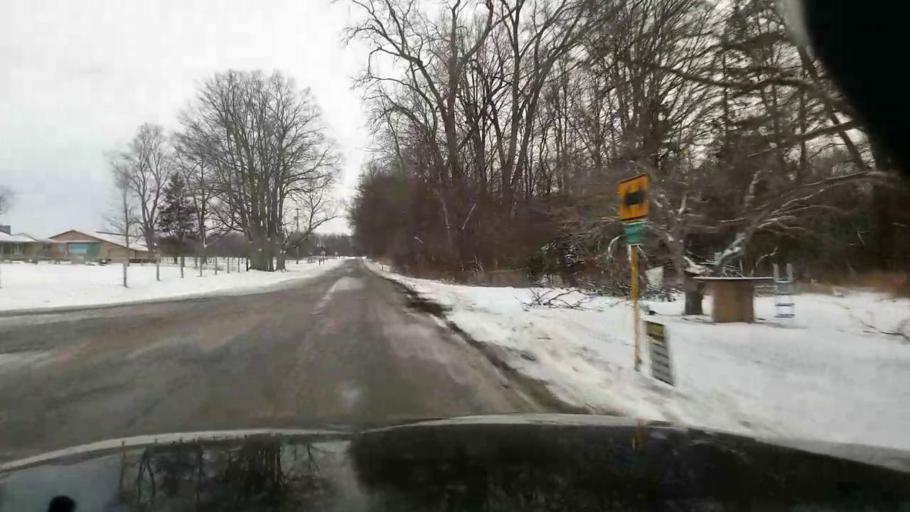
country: US
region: Michigan
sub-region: Jackson County
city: Vandercook Lake
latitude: 42.0941
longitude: -84.4657
